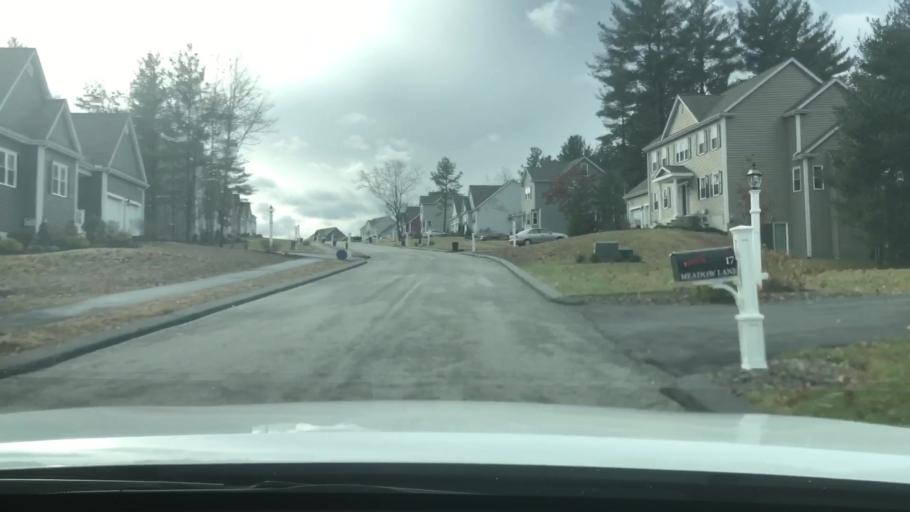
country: US
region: Massachusetts
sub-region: Worcester County
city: Blackstone
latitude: 42.0377
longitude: -71.5160
